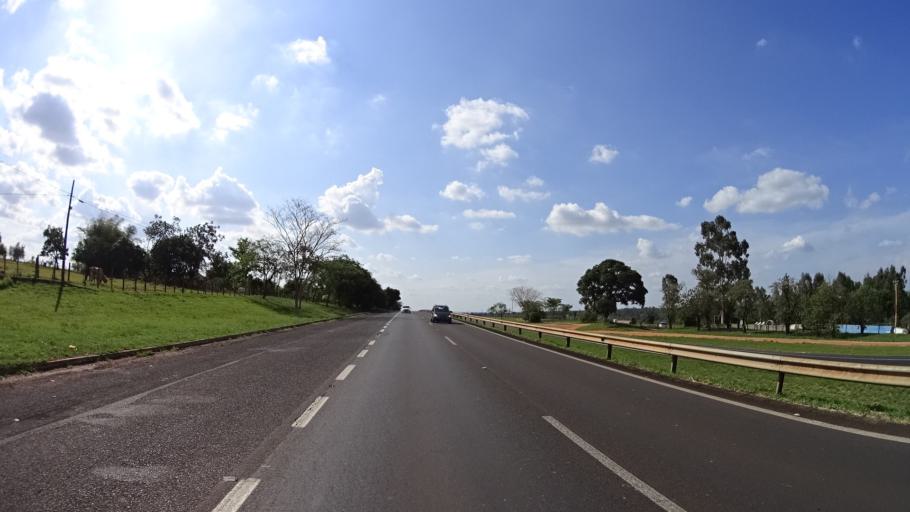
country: BR
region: Sao Paulo
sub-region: Guapiacu
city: Guapiacu
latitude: -20.9205
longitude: -49.2818
